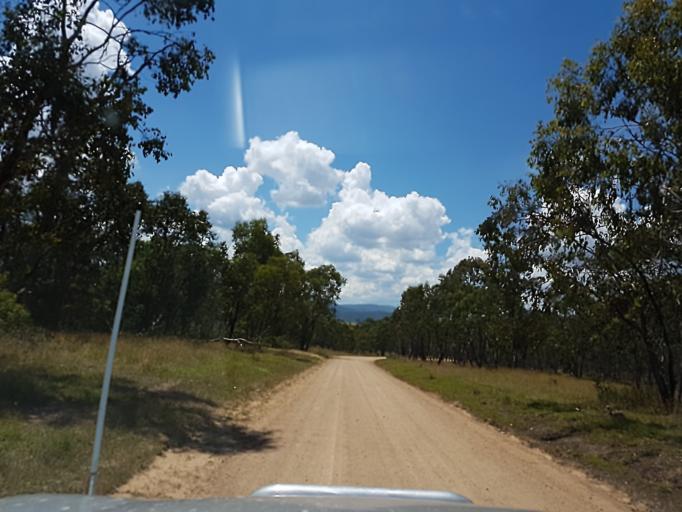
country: AU
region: Victoria
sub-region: Alpine
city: Mount Beauty
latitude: -36.9001
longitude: 147.8304
